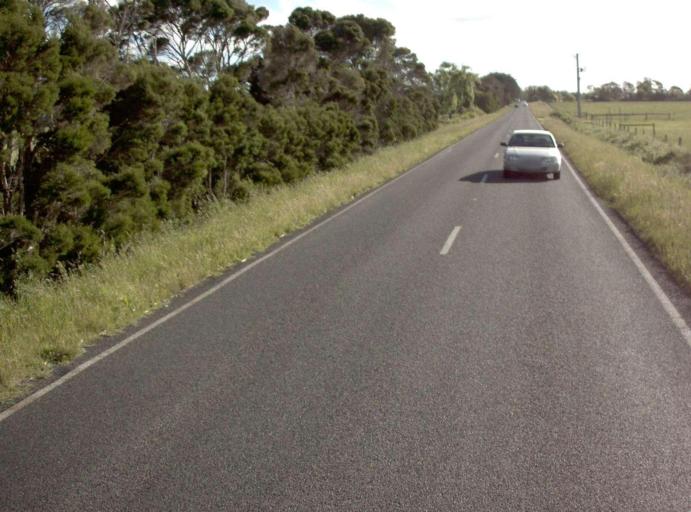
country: AU
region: Victoria
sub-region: Bass Coast
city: North Wonthaggi
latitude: -38.5173
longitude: 145.8973
